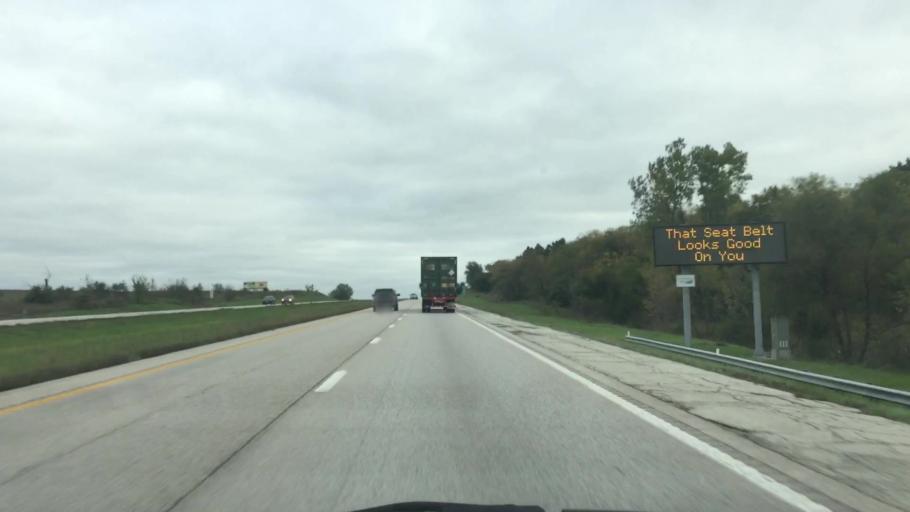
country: US
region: Missouri
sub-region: Clinton County
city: Cameron
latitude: 39.6891
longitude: -94.2302
